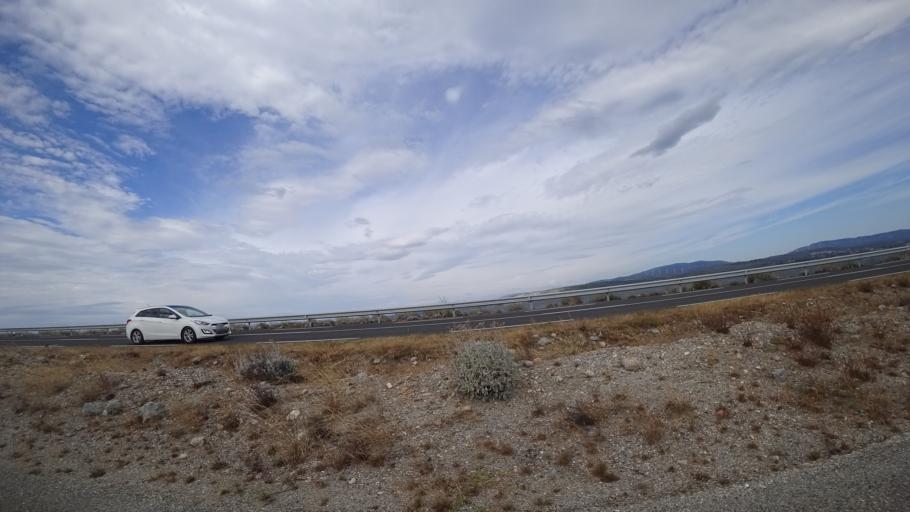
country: FR
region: Languedoc-Roussillon
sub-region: Departement de l'Aude
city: Leucate
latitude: 42.8617
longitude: 3.0297
